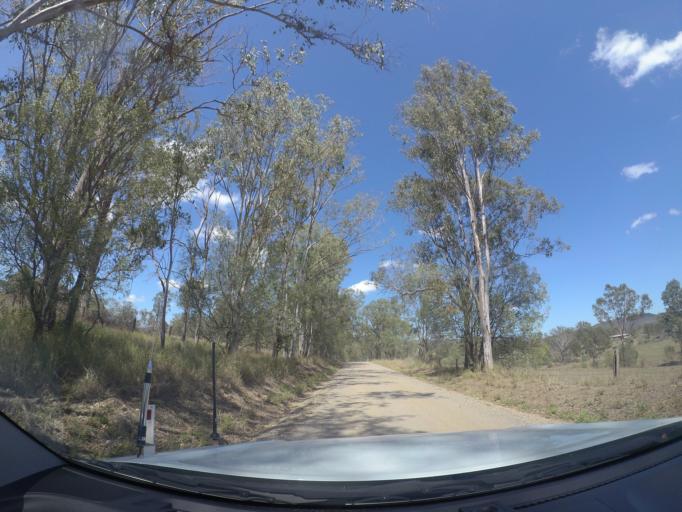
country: AU
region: Queensland
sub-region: Logan
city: Cedar Vale
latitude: -27.8480
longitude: 152.8963
